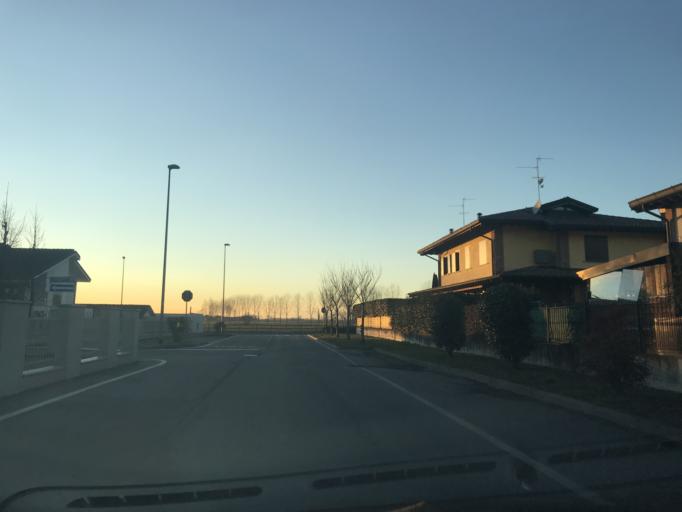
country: IT
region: Lombardy
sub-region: Provincia di Lodi
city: Pieve Fissiraga
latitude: 45.2639
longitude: 9.4573
